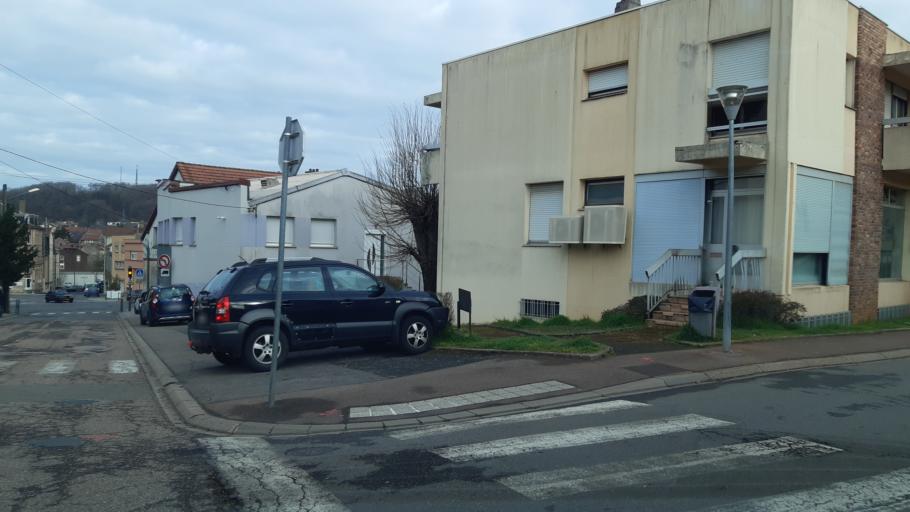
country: FR
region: Lorraine
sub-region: Departement de la Moselle
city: Audun-le-Tiche
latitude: 49.4765
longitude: 5.9594
